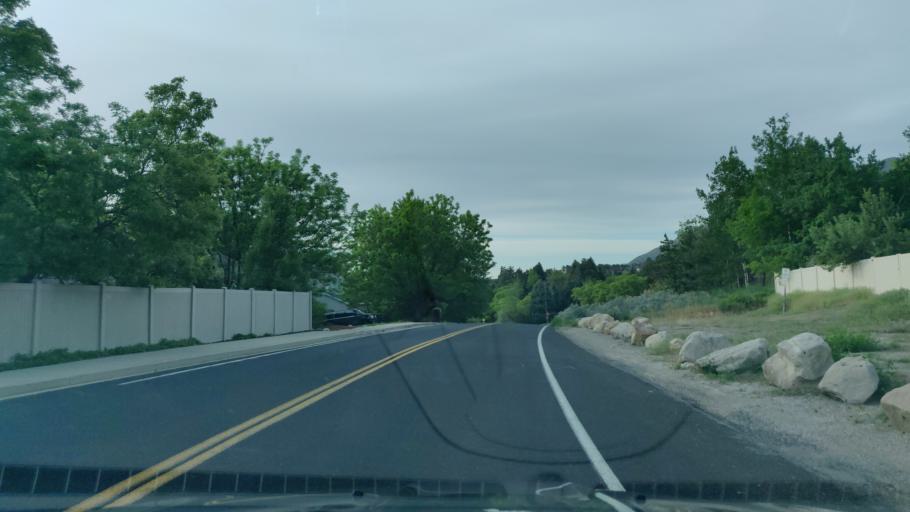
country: US
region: Utah
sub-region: Salt Lake County
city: Granite
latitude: 40.5918
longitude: -111.8000
